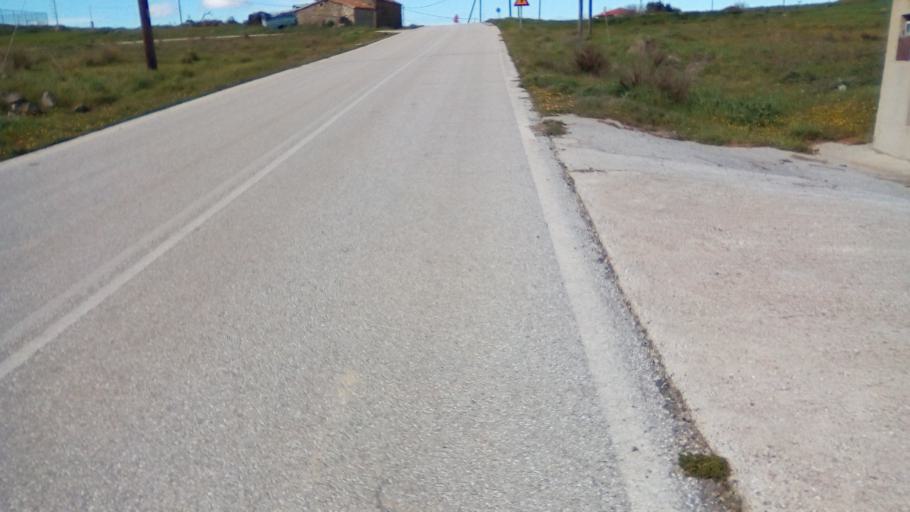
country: GR
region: North Aegean
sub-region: Nomos Lesvou
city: Myrina
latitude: 39.9294
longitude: 25.2320
